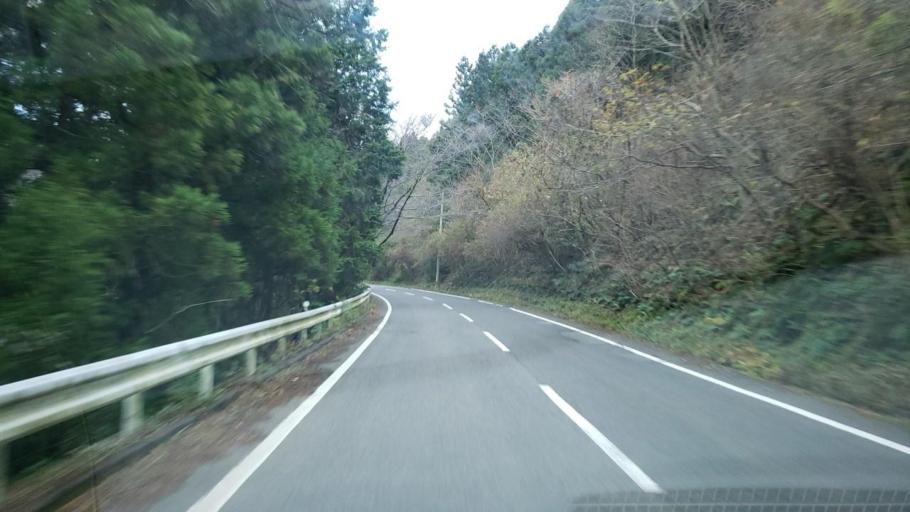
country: JP
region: Tokushima
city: Wakimachi
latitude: 34.1857
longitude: 134.2008
